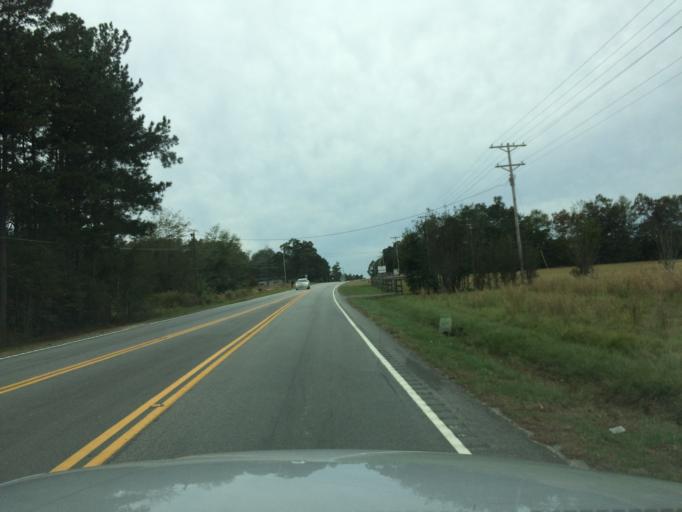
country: US
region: South Carolina
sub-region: Aiken County
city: New Ellenton
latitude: 33.3926
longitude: -81.7186
